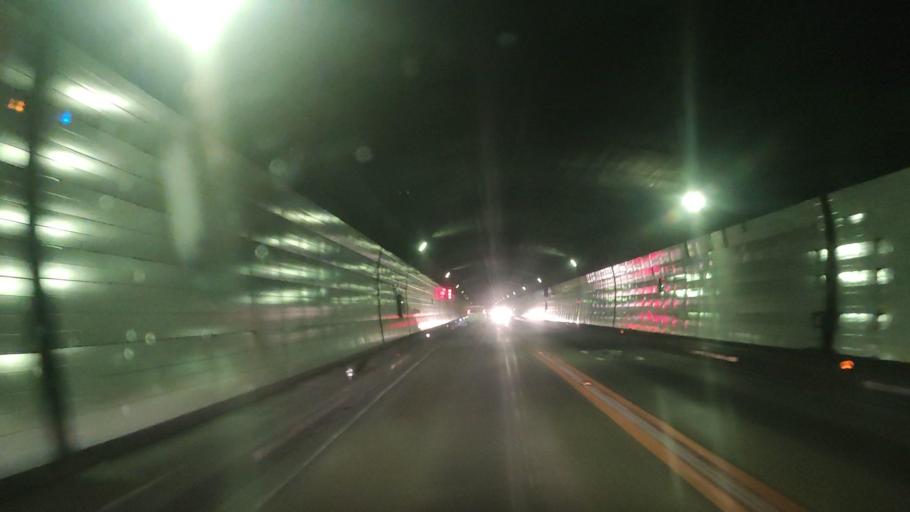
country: JP
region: Kumamoto
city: Hitoyoshi
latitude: 32.0994
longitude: 130.8039
